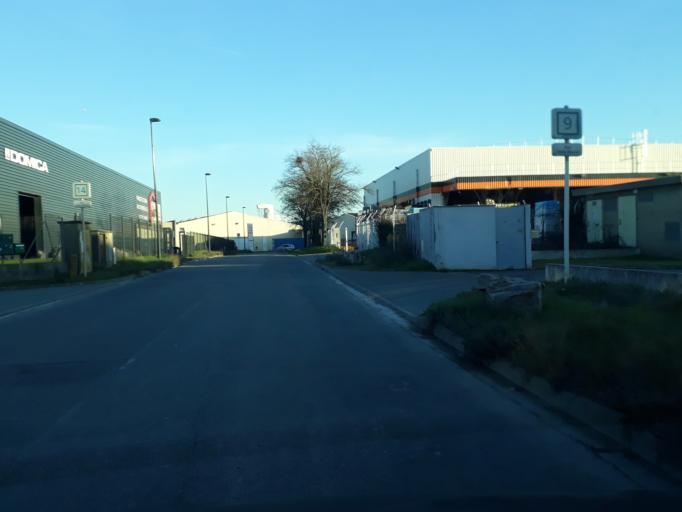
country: FR
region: Midi-Pyrenees
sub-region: Departement de la Haute-Garonne
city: Portet-sur-Garonne
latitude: 43.5527
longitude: 1.4166
